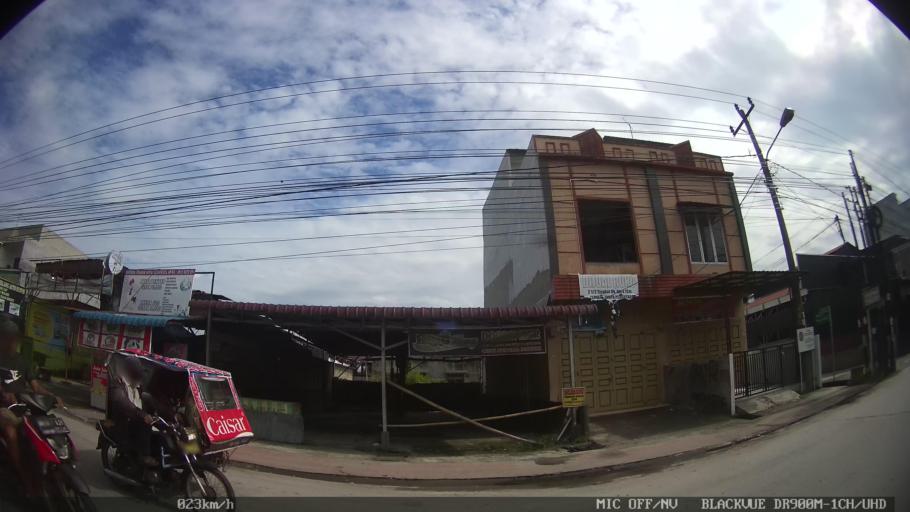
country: ID
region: North Sumatra
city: Sunggal
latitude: 3.6056
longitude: 98.6224
